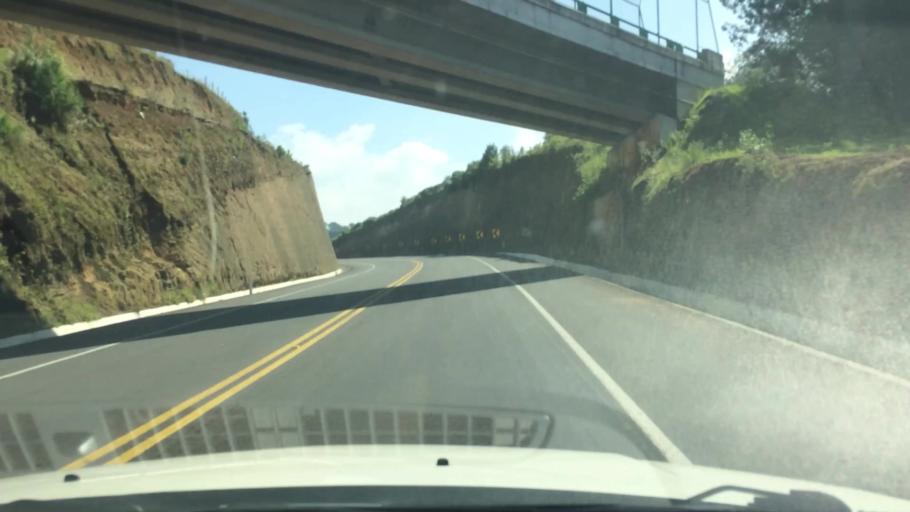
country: MX
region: Mexico
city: Amanalco de Becerra
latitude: 19.2967
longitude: -100.0147
